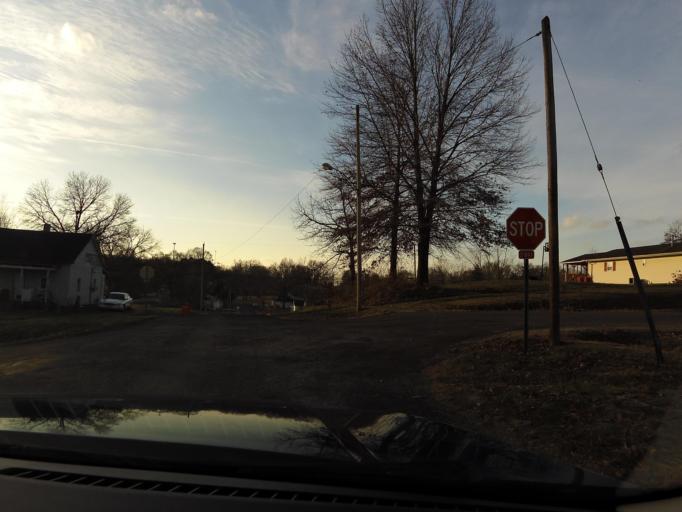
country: US
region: Illinois
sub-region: Fayette County
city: Vandalia
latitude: 38.9599
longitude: -89.1048
